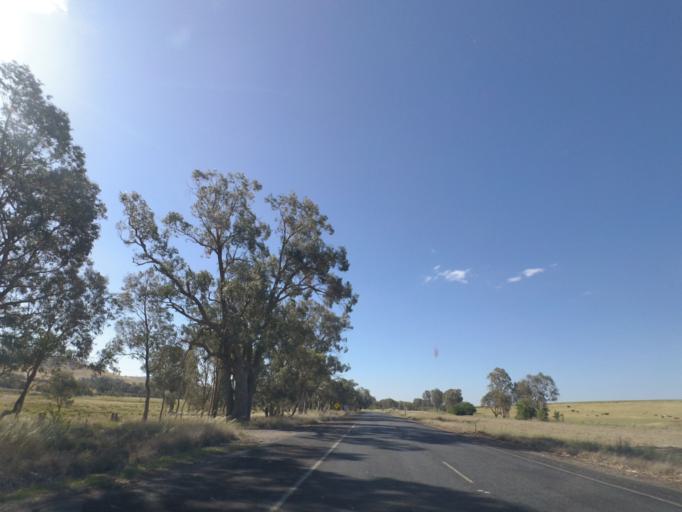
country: AU
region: New South Wales
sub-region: Greater Hume Shire
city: Holbrook
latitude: -35.7890
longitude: 147.2758
